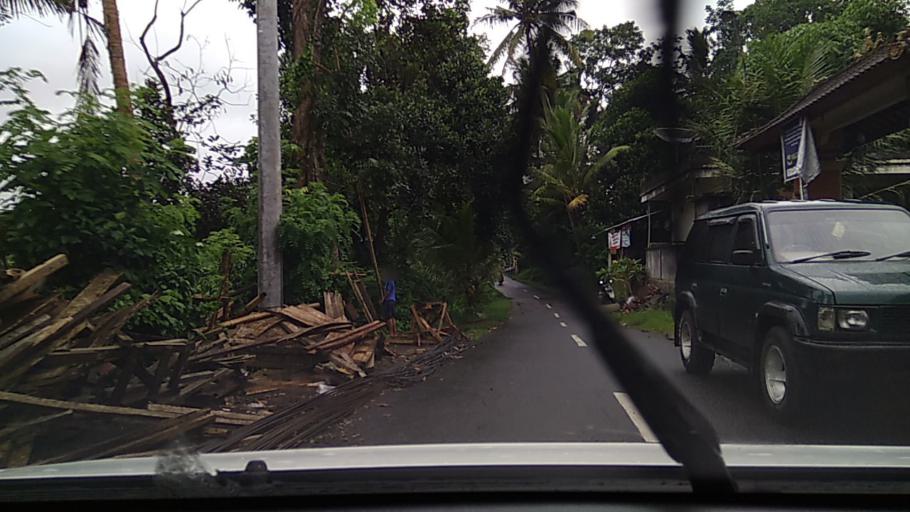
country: ID
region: Bali
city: Tiyingtali Kelod
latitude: -8.4001
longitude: 115.6183
